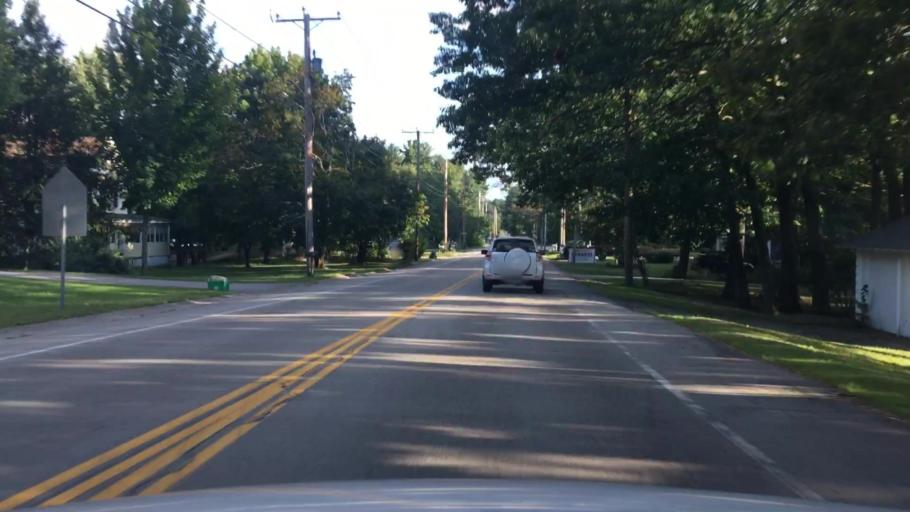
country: US
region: Maine
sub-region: York County
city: Eliot
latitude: 43.1503
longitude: -70.8397
